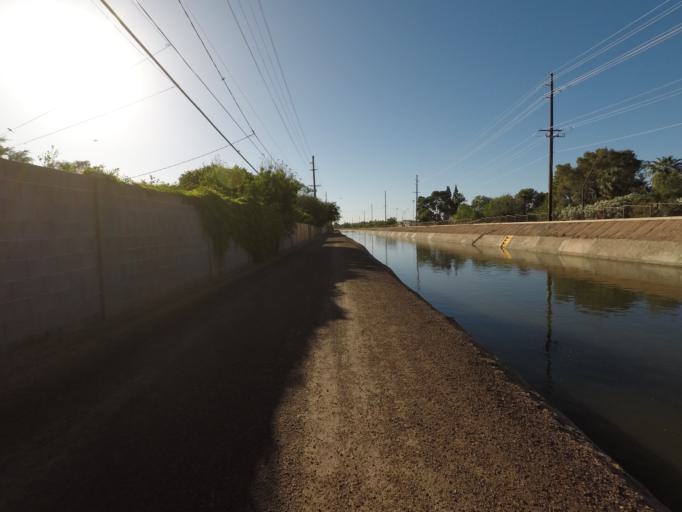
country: US
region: Arizona
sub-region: Maricopa County
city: Paradise Valley
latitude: 33.4918
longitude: -111.9682
